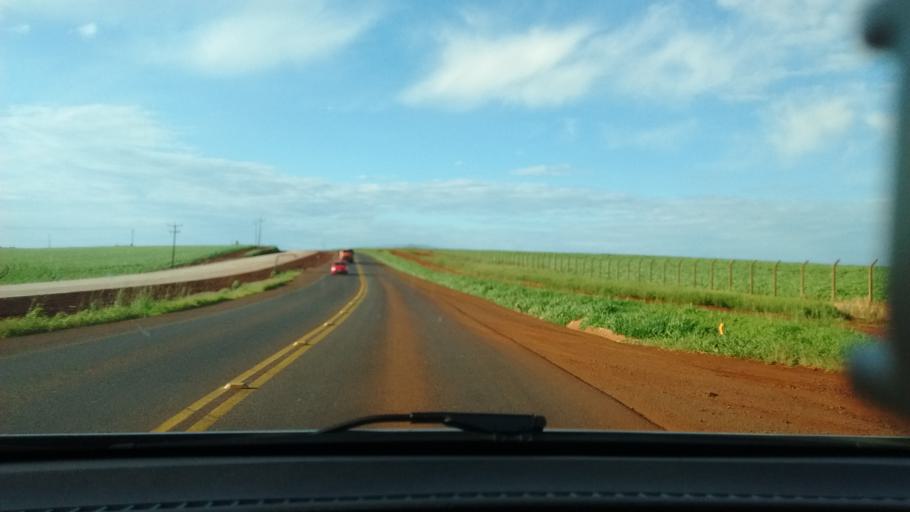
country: BR
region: Parana
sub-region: Cascavel
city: Cascavel
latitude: -25.1239
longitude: -53.5874
